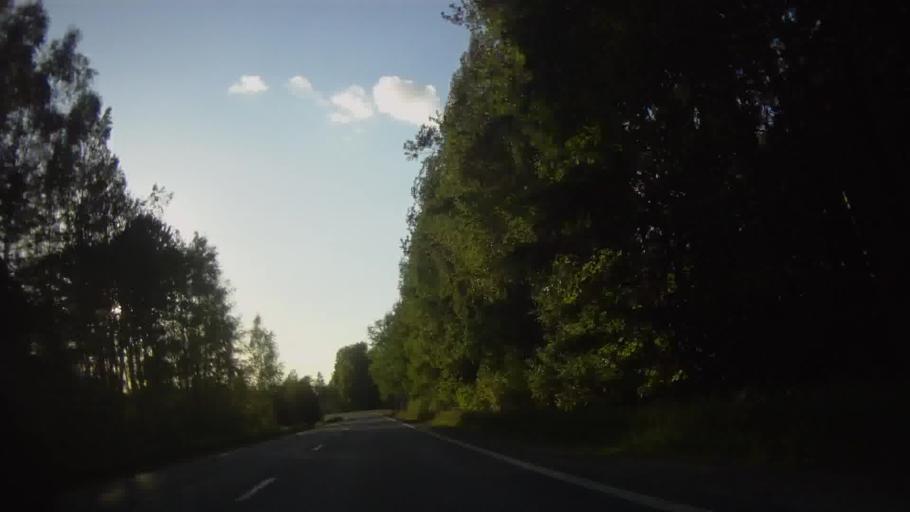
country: LV
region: Livani
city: Livani
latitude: 56.5266
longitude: 26.1548
